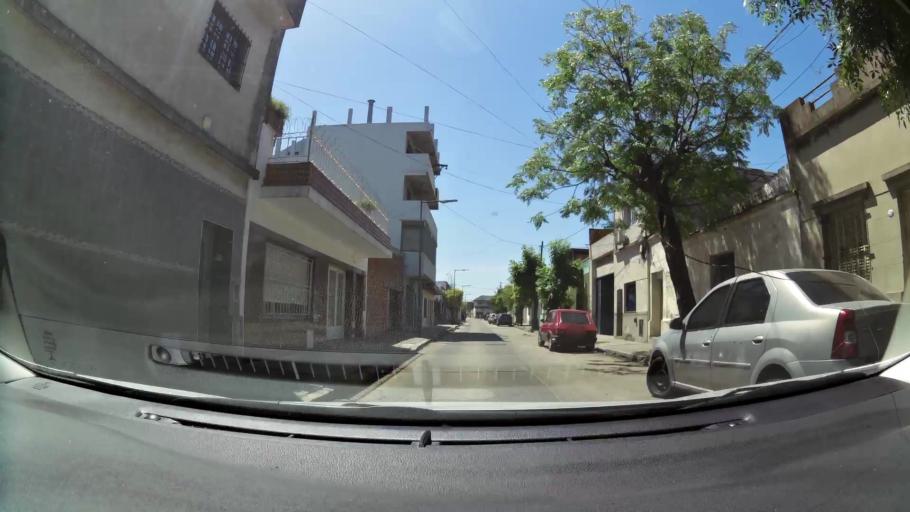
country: AR
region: Buenos Aires
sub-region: Partido de Avellaneda
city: Avellaneda
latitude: -34.6526
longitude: -58.4063
